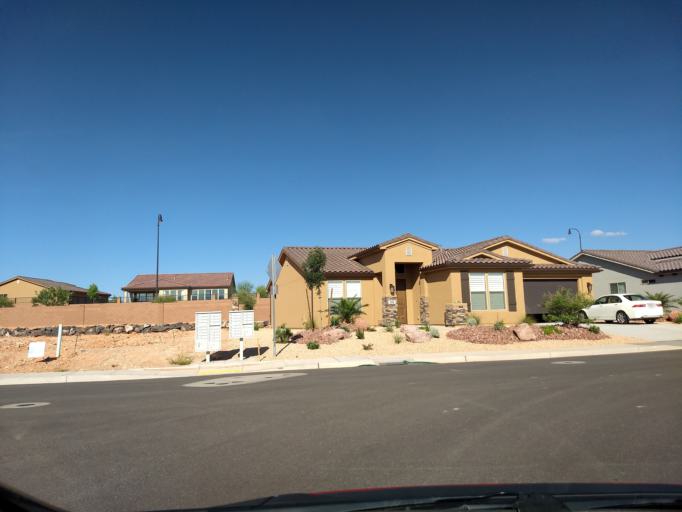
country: US
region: Utah
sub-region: Washington County
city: Washington
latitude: 37.1430
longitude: -113.5162
